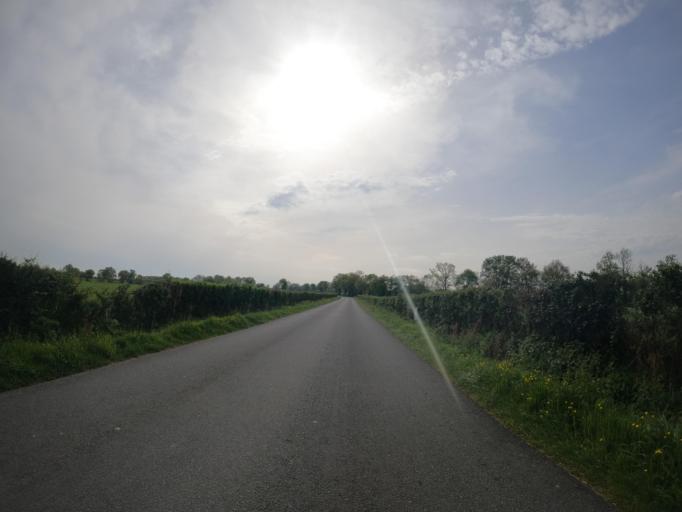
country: FR
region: Poitou-Charentes
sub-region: Departement des Deux-Sevres
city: Moncoutant
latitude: 46.6978
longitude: -0.5485
